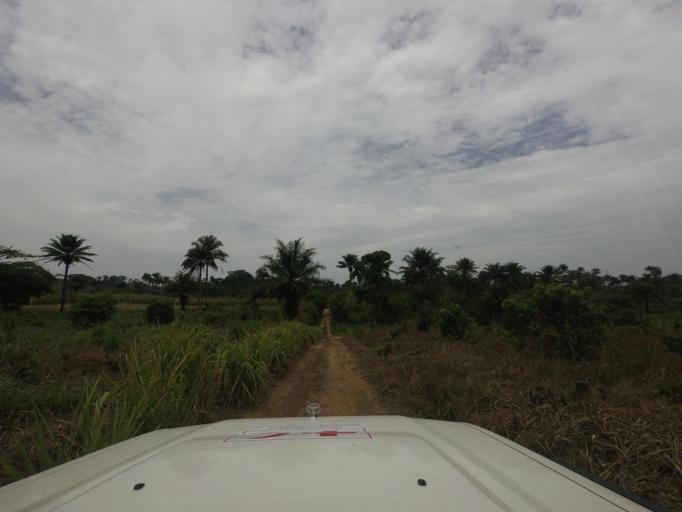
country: SL
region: Eastern Province
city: Buedu
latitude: 8.4242
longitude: -10.2631
